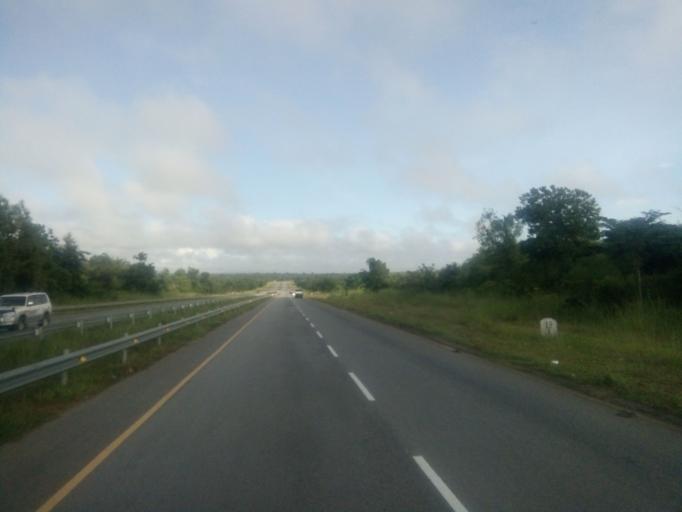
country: MM
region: Bago
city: Thanatpin
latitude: 17.3164
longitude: 96.2176
